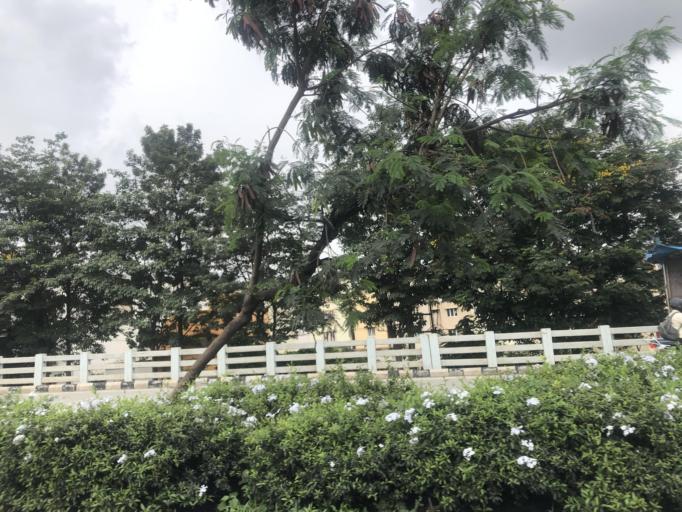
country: IN
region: Karnataka
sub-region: Bangalore Urban
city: Bangalore
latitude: 12.9672
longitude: 77.5125
